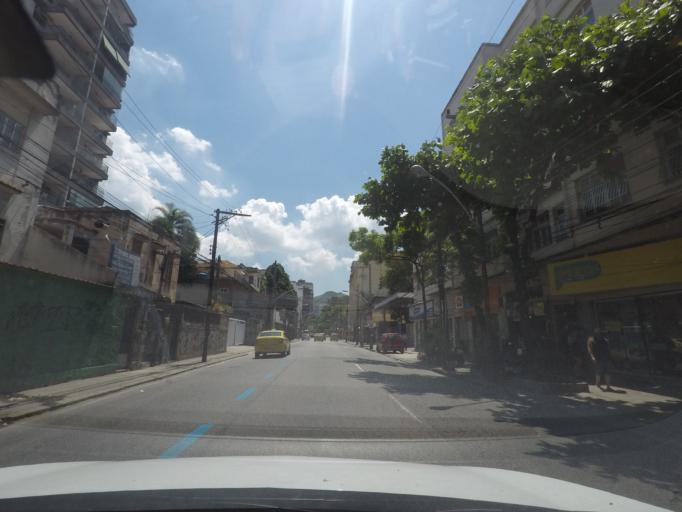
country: BR
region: Rio de Janeiro
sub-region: Rio De Janeiro
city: Rio de Janeiro
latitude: -22.9162
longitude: -43.2527
